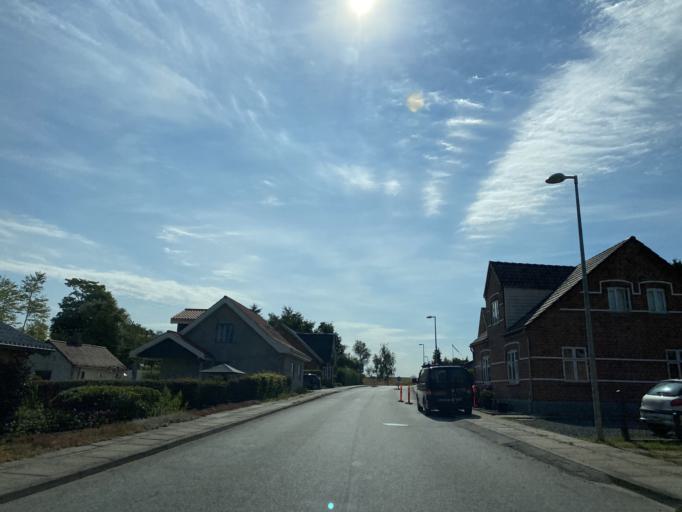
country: DK
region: Central Jutland
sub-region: Favrskov Kommune
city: Hammel
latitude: 56.2958
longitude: 9.7966
